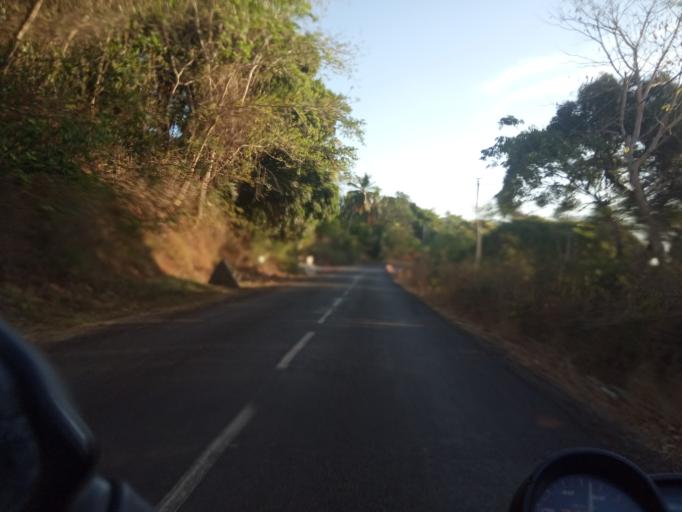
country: YT
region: Kani-Keli
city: Kani Keli
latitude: -12.9359
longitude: 45.1034
